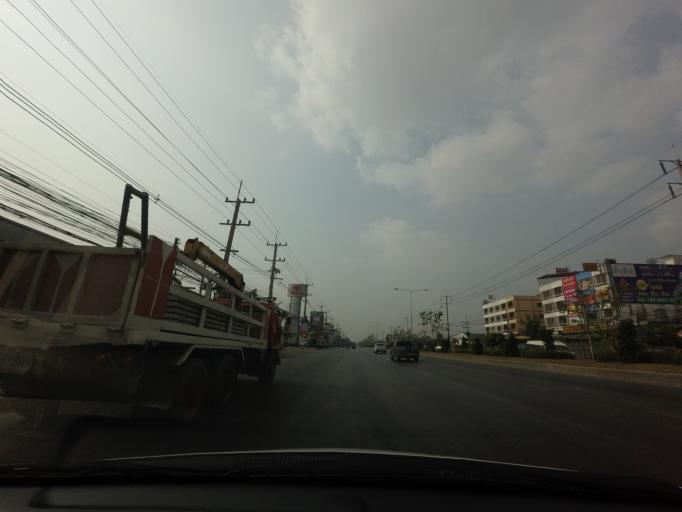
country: TH
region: Bangkok
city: Nong Khaem
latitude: 13.7389
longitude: 100.3295
